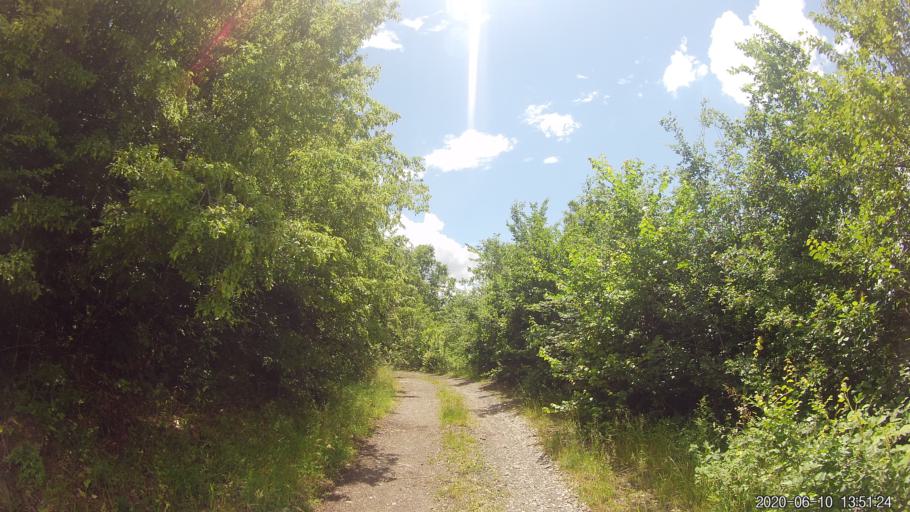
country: XK
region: Prizren
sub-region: Komuna e Therandes
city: Budakovo
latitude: 42.4054
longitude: 20.9261
